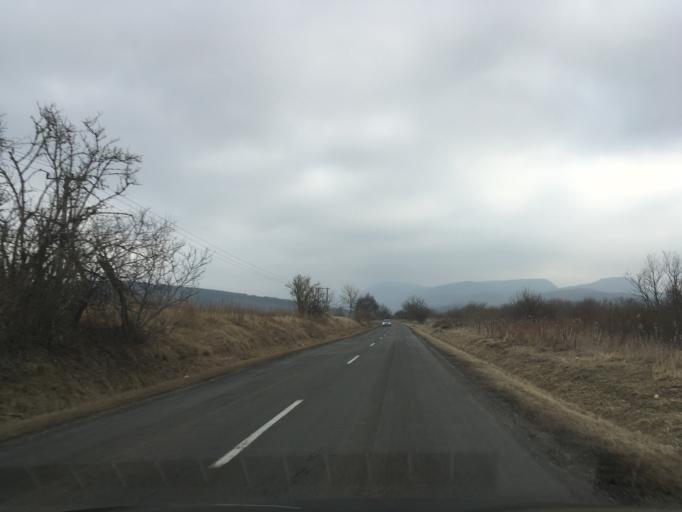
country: HU
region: Komarom-Esztergom
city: Esztergom
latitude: 47.7603
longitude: 18.7650
